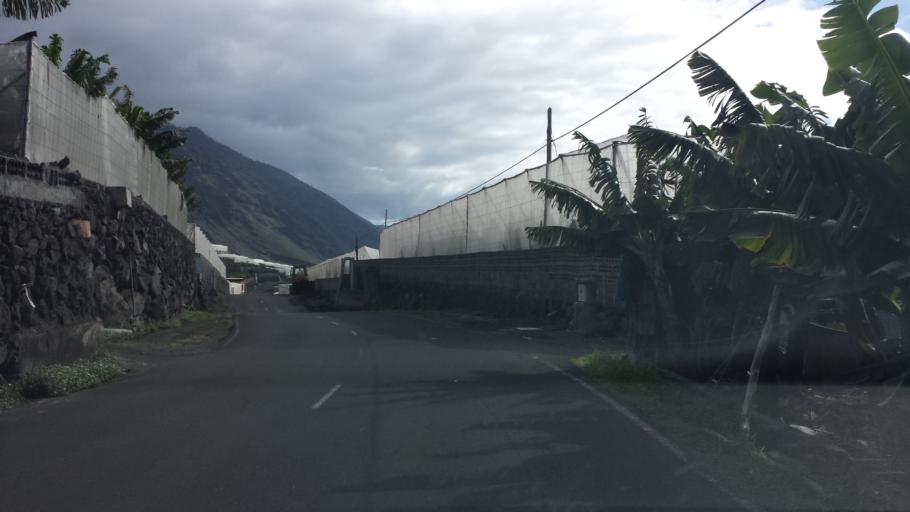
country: ES
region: Canary Islands
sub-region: Provincia de Santa Cruz de Tenerife
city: El Paso
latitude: 28.5687
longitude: -17.8947
